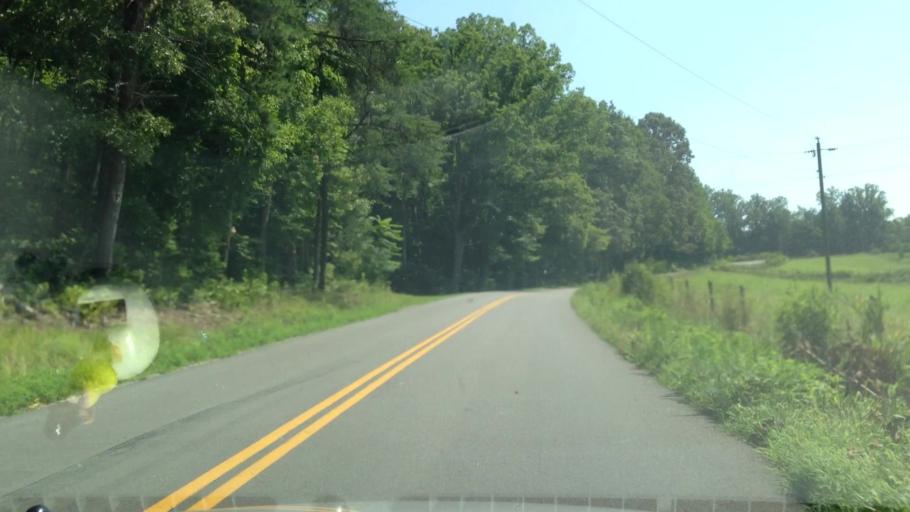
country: US
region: Virginia
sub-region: Patrick County
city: Patrick Springs
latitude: 36.5749
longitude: -80.1952
